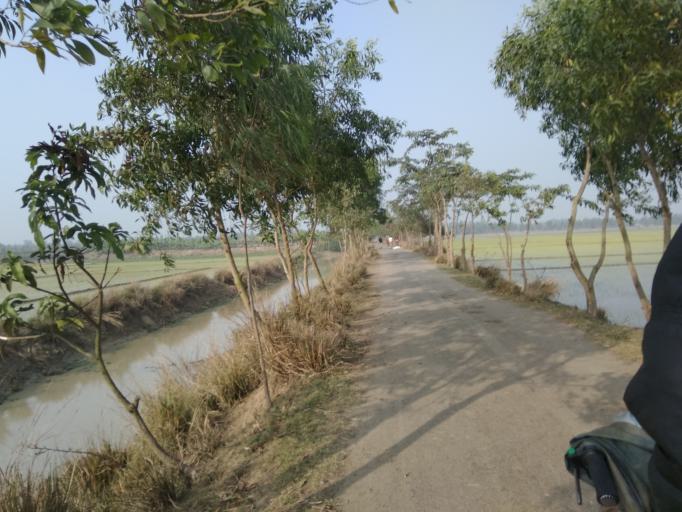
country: BD
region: Rajshahi
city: Bogra
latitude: 24.4710
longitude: 89.2685
